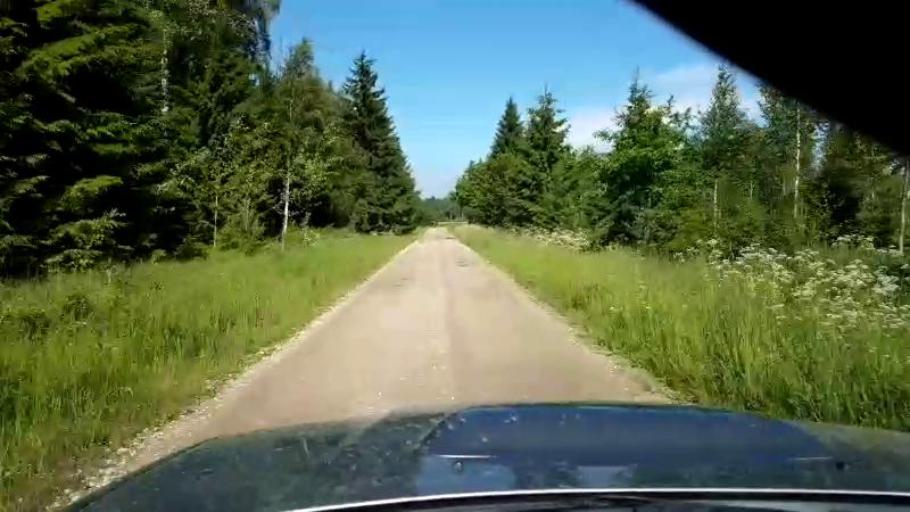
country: EE
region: Paernumaa
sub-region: Sindi linn
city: Sindi
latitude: 58.5096
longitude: 24.6893
